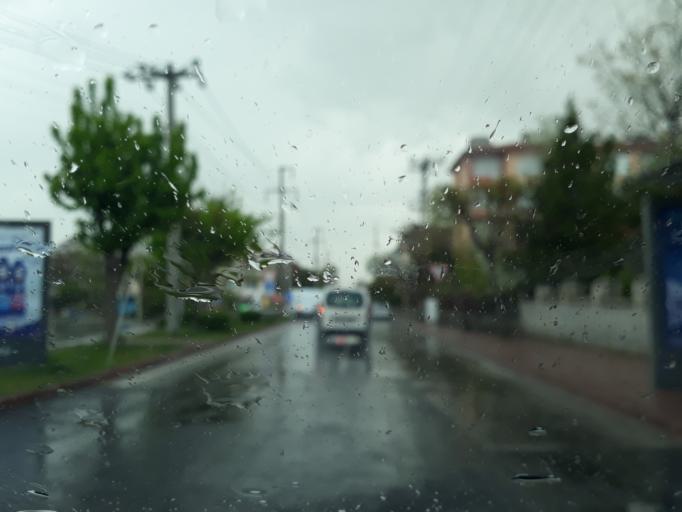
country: TR
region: Konya
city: Selcuklu
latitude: 37.9143
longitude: 32.4953
